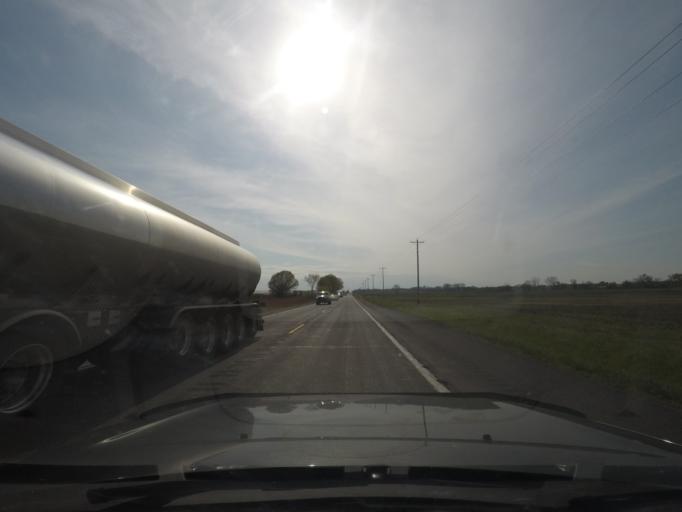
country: US
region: Michigan
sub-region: Berrien County
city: Three Oaks
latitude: 41.7983
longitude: -86.5476
